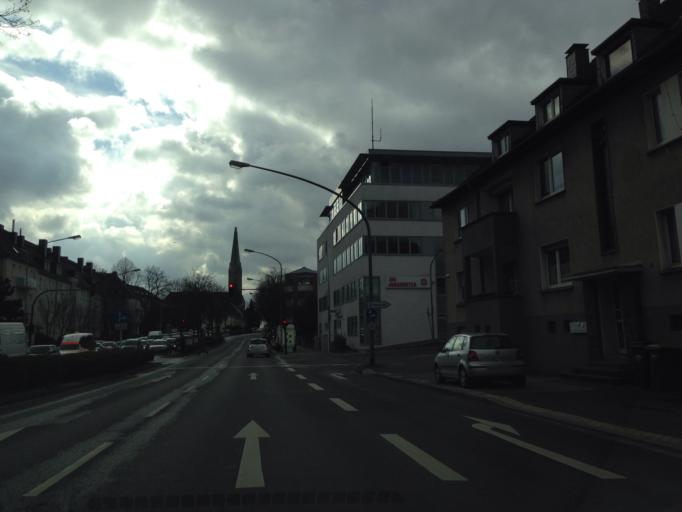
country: DE
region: North Rhine-Westphalia
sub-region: Regierungsbezirk Dusseldorf
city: Essen
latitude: 51.4422
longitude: 7.0332
